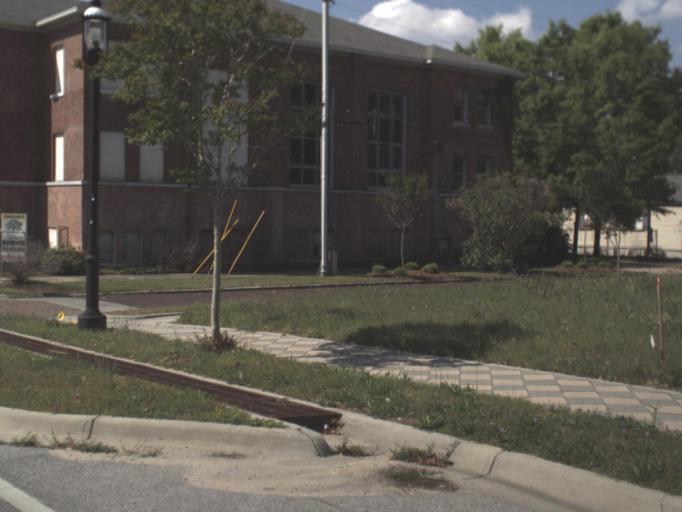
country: US
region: Florida
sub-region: Escambia County
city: Pensacola
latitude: 30.4196
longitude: -87.2116
